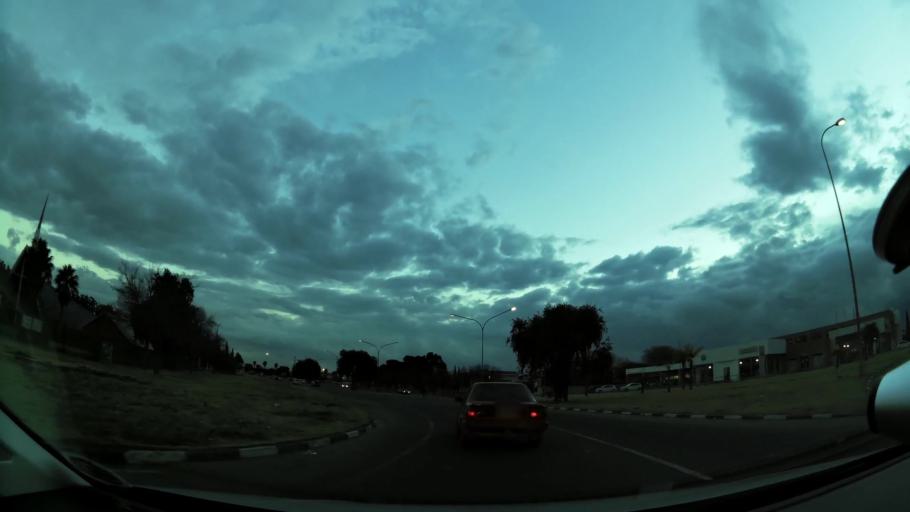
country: ZA
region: Orange Free State
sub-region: Lejweleputswa District Municipality
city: Welkom
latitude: -27.9775
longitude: 26.7443
